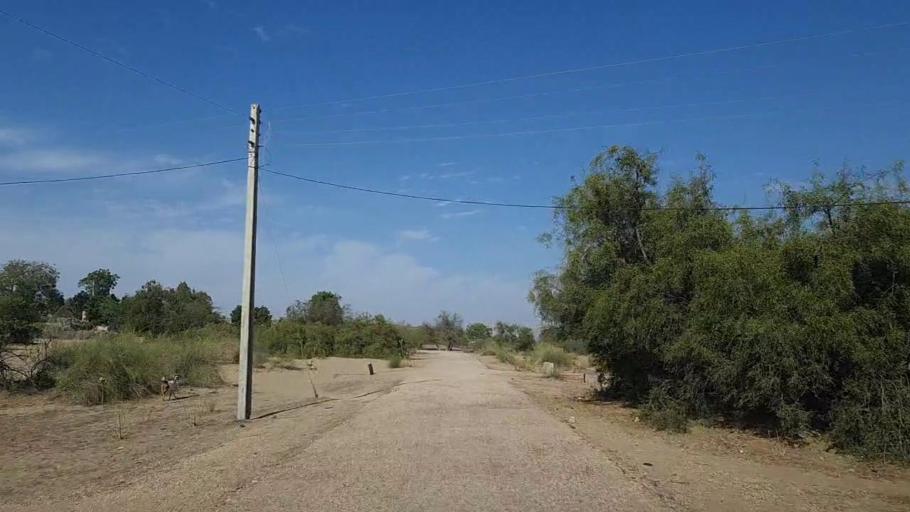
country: PK
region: Sindh
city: Naukot
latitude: 24.8483
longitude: 69.5476
